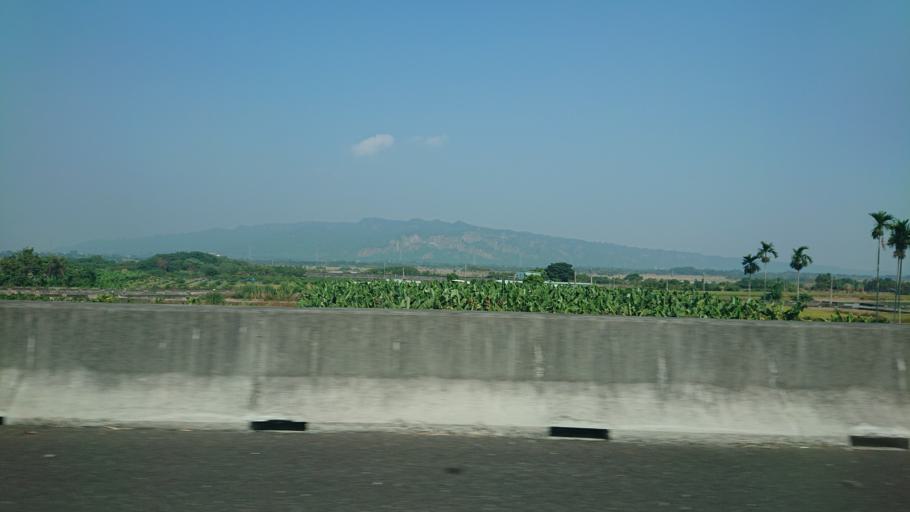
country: TW
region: Taiwan
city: Lugu
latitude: 23.7750
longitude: 120.6646
